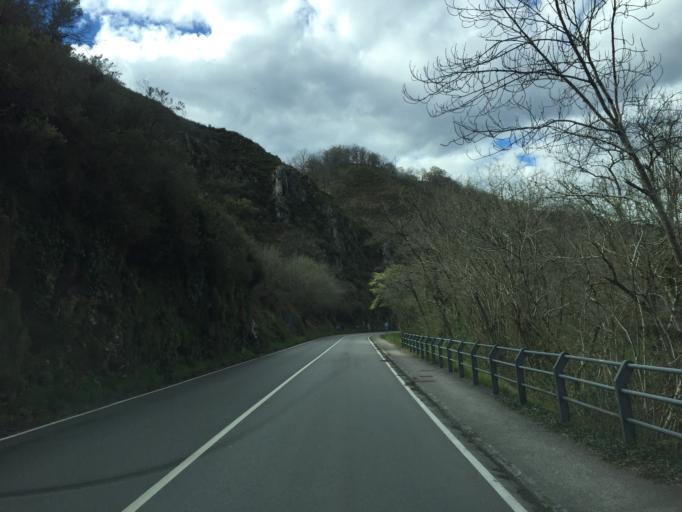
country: ES
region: Asturias
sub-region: Province of Asturias
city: Cangas de Onis
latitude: 43.3315
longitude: -5.0815
